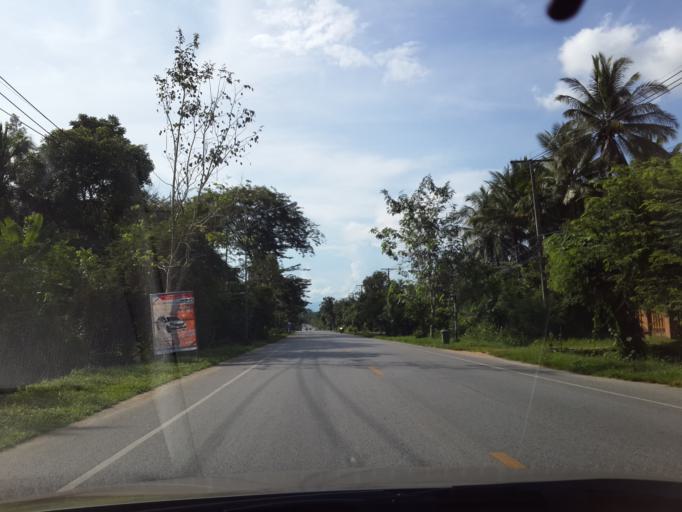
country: TH
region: Yala
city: Yala
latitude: 6.4932
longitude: 101.3034
